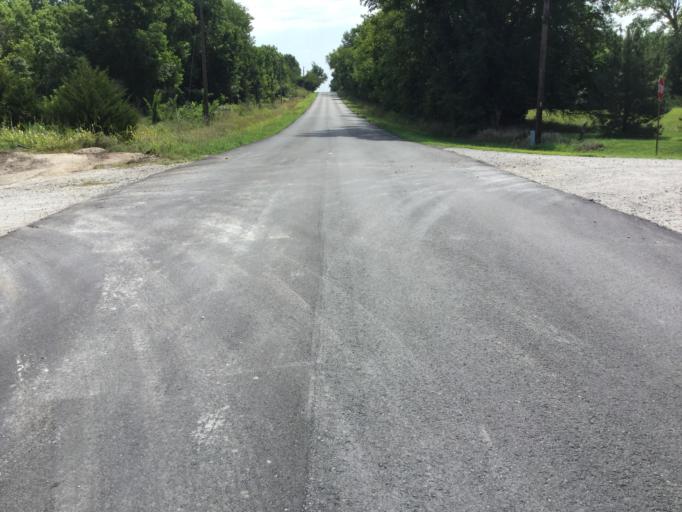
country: US
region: Kansas
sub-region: Montgomery County
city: Coffeyville
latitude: 37.0346
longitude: -95.5504
